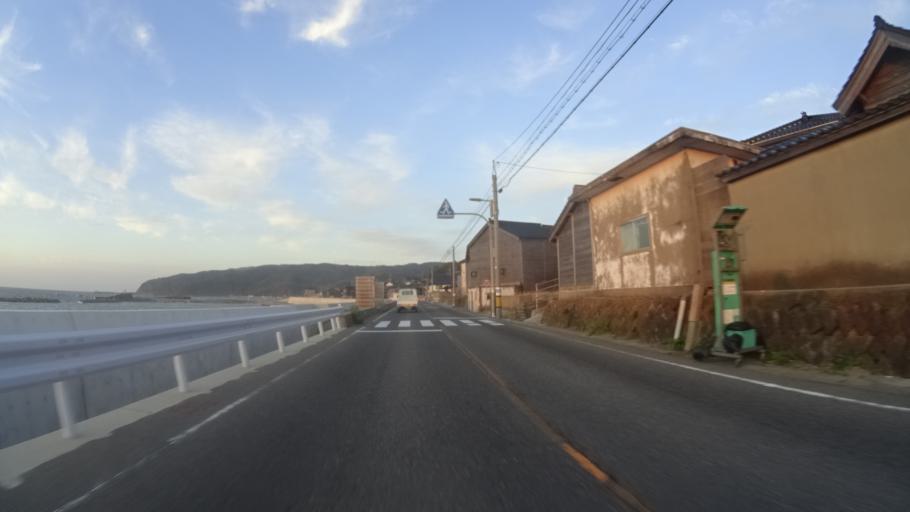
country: JP
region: Ishikawa
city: Nanao
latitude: 37.2779
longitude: 136.7334
